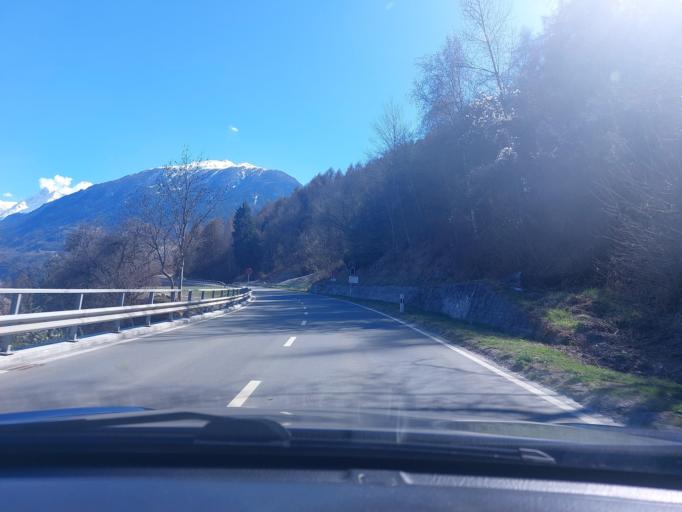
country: CH
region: Valais
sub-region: Herens District
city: Heremence
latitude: 46.1973
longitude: 7.4061
